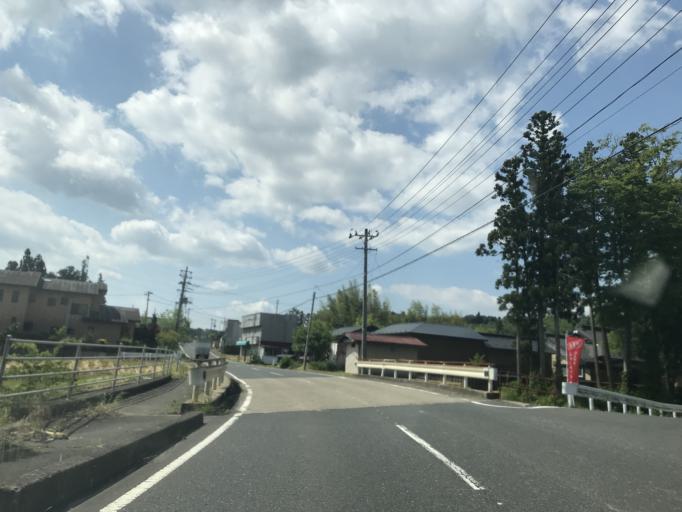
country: JP
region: Miyagi
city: Furukawa
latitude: 38.7861
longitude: 140.9580
